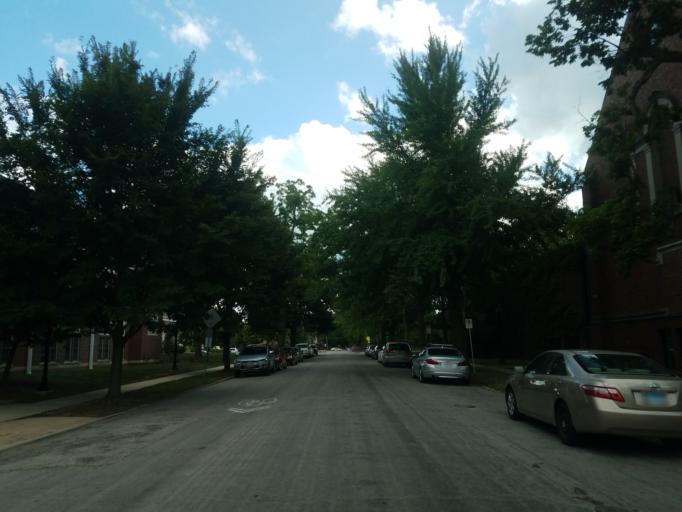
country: US
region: Illinois
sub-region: McLean County
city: Bloomington
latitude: 40.4901
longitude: -88.9901
